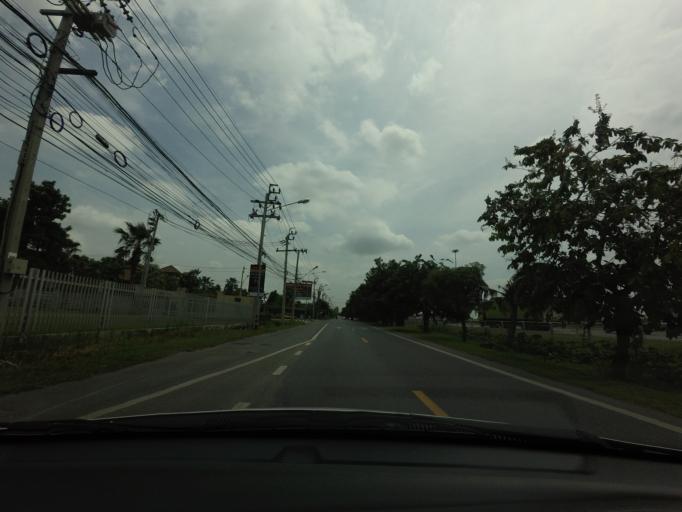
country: TH
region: Bangkok
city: Khan Na Yao
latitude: 13.8625
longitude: 100.6771
